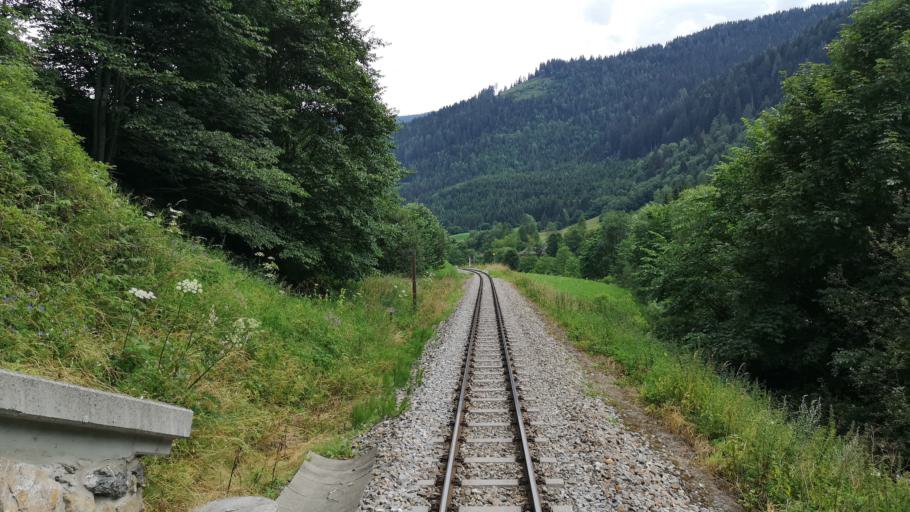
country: AT
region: Salzburg
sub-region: Politischer Bezirk Tamsweg
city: Ramingstein
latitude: 47.0679
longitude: 13.8876
